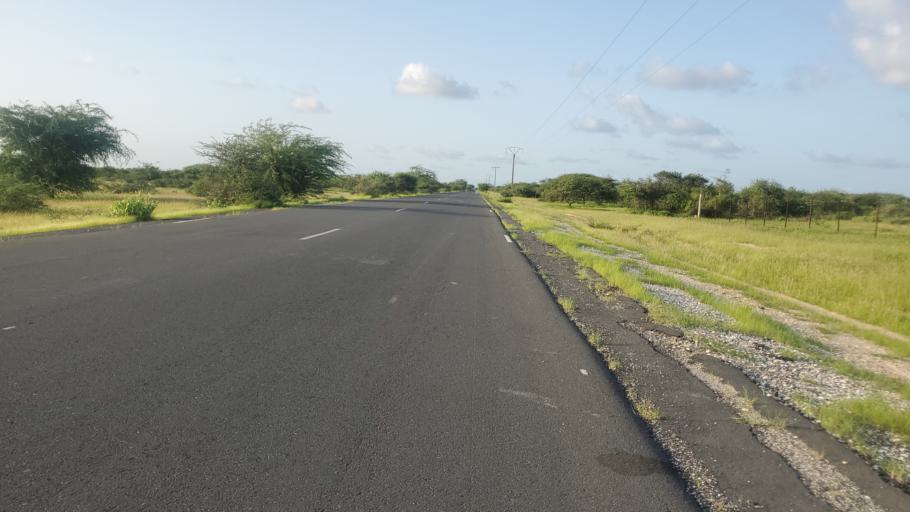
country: SN
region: Saint-Louis
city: Saint-Louis
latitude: 16.1757
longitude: -16.4096
